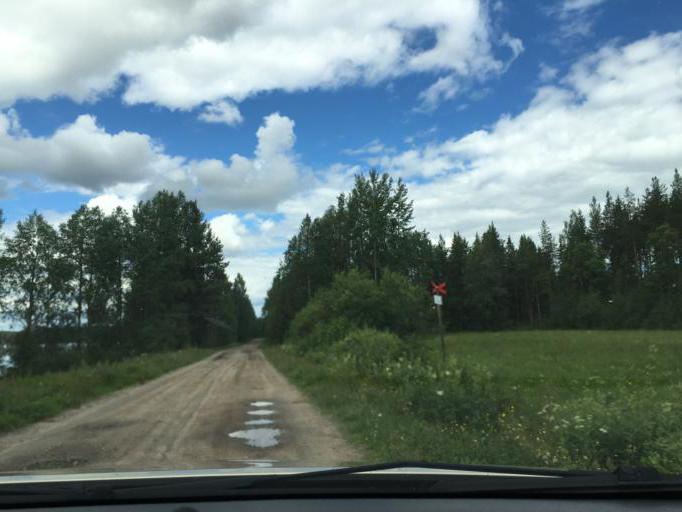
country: SE
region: Norrbotten
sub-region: Overkalix Kommun
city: OEverkalix
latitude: 66.1231
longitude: 22.7857
